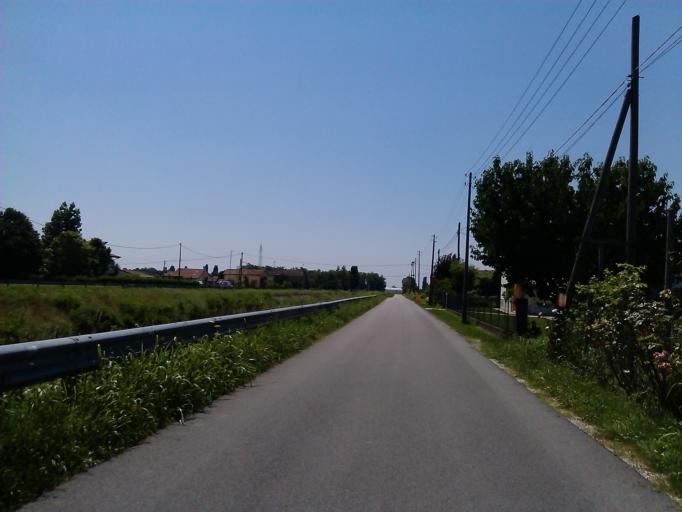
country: IT
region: Veneto
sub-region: Provincia di Treviso
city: Sant'Andrea
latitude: 45.6437
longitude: 11.9225
